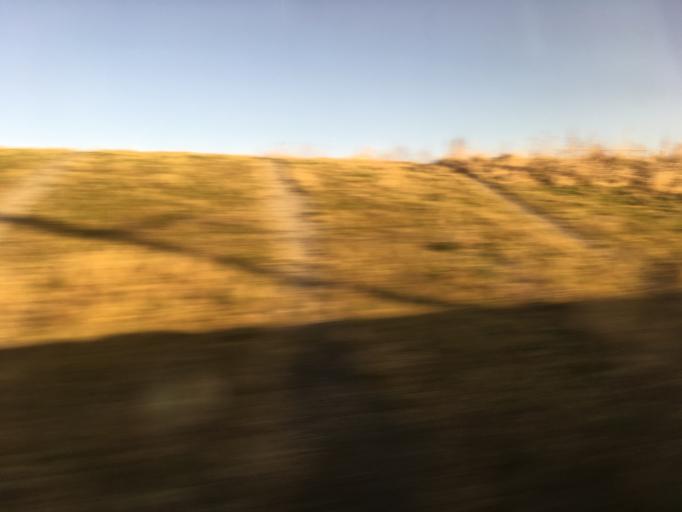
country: GB
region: England
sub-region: Wiltshire
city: Lyneham
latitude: 51.5541
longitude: -1.9534
